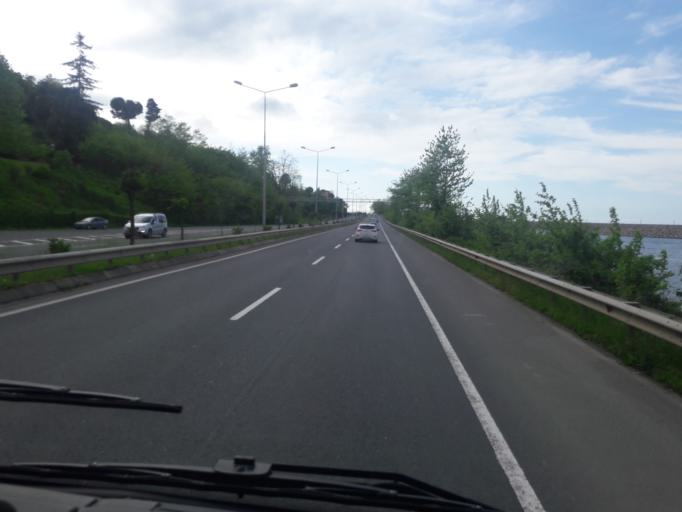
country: TR
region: Giresun
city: Piraziz
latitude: 40.9591
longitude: 38.1084
